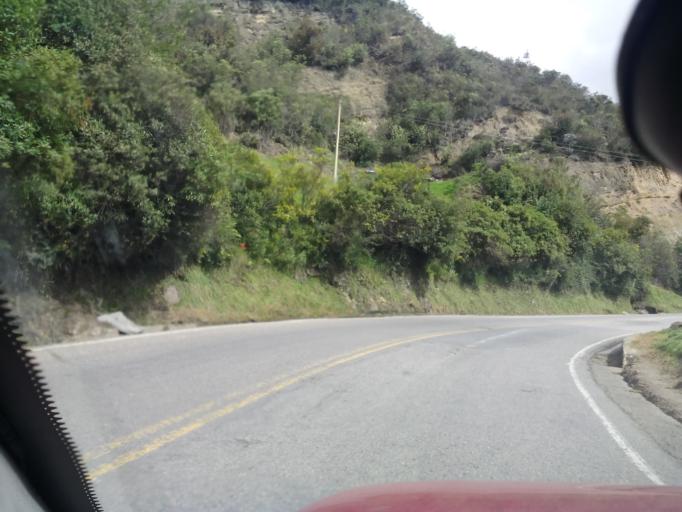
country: CO
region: Boyaca
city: Combita
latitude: 5.6828
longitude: -73.3641
